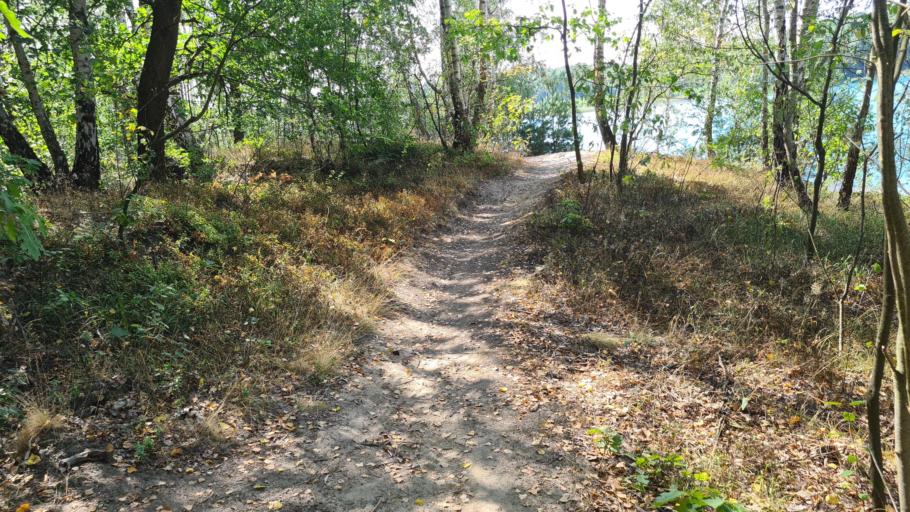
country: DE
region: Brandenburg
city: Sallgast
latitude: 51.5732
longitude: 13.8435
